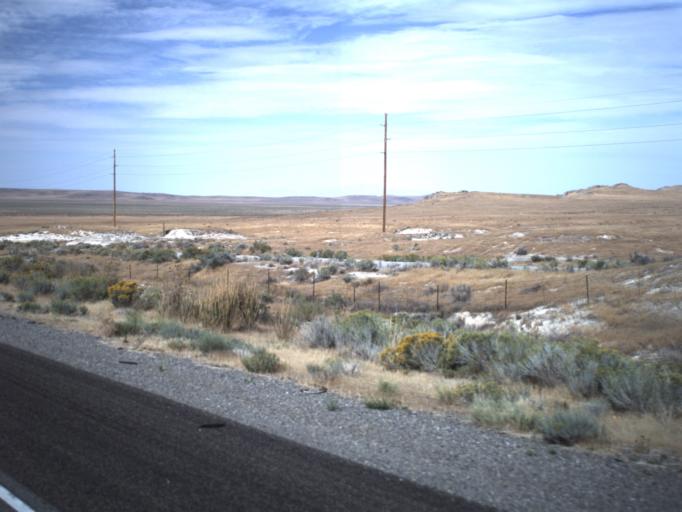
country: US
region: Utah
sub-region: Tooele County
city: Grantsville
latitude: 40.7583
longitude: -113.0197
